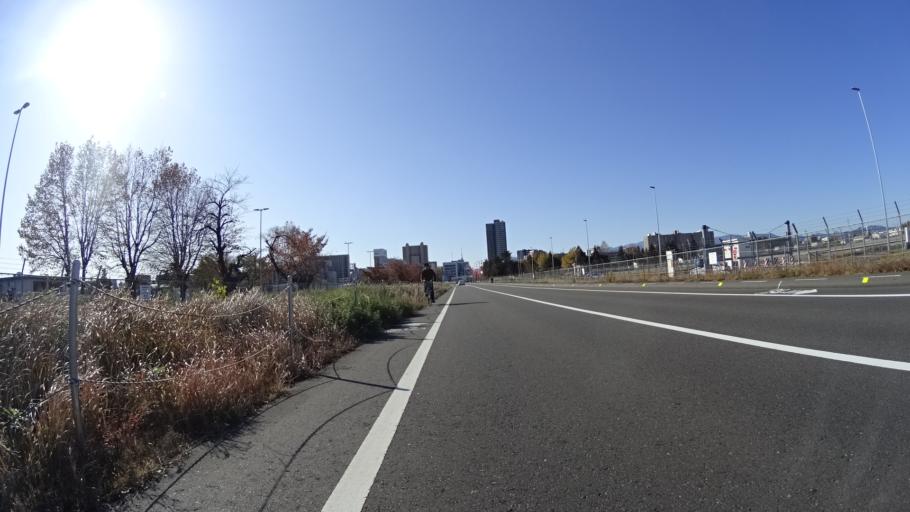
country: JP
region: Tokyo
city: Hachioji
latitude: 35.5851
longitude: 139.3751
